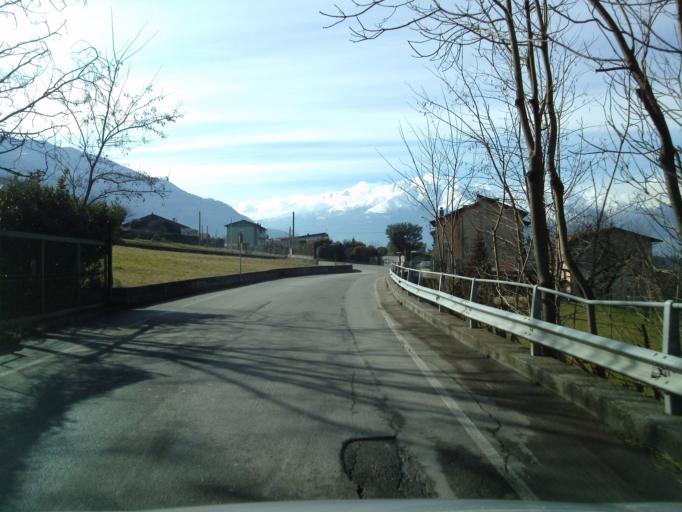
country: IT
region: Lombardy
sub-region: Provincia di Lecco
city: Colico Piano
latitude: 46.1343
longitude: 9.3837
